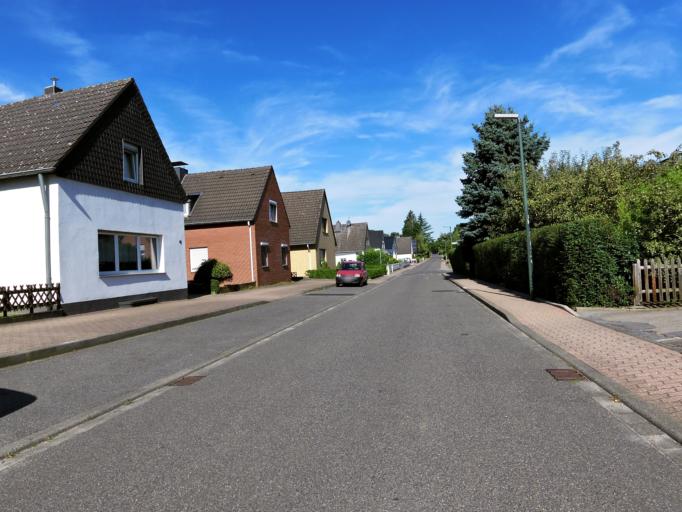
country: DE
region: North Rhine-Westphalia
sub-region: Regierungsbezirk Koln
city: Alsdorf
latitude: 50.8519
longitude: 6.2065
